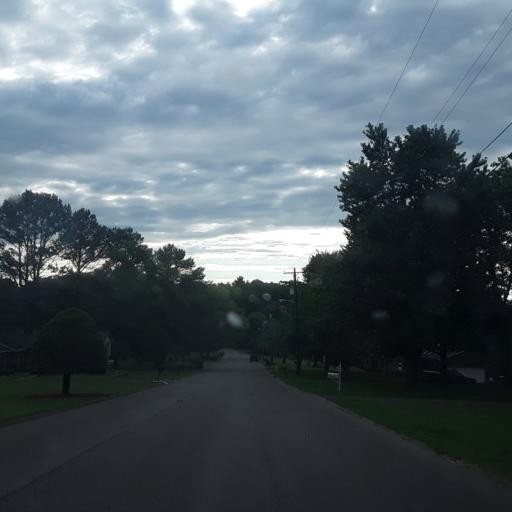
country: US
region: Tennessee
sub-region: Wilson County
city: Green Hill
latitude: 36.1688
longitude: -86.5883
